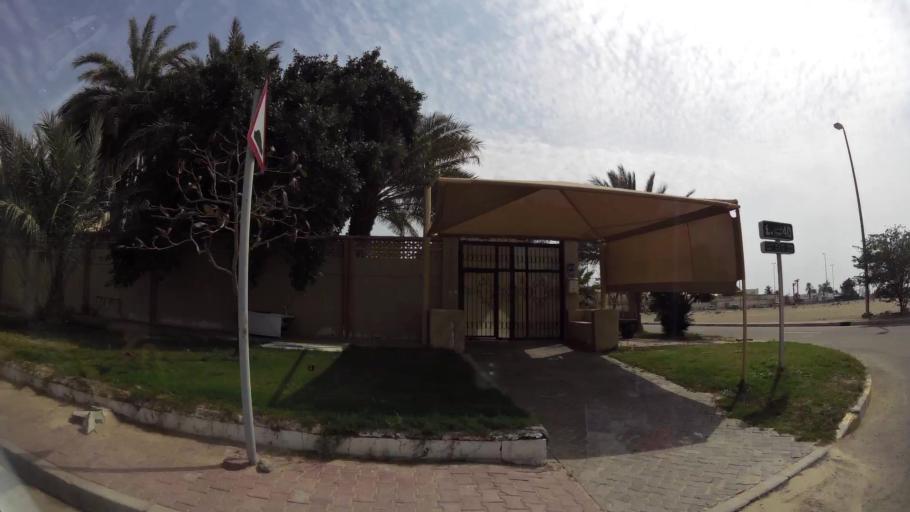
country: AE
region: Abu Dhabi
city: Abu Dhabi
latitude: 24.5540
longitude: 54.6791
